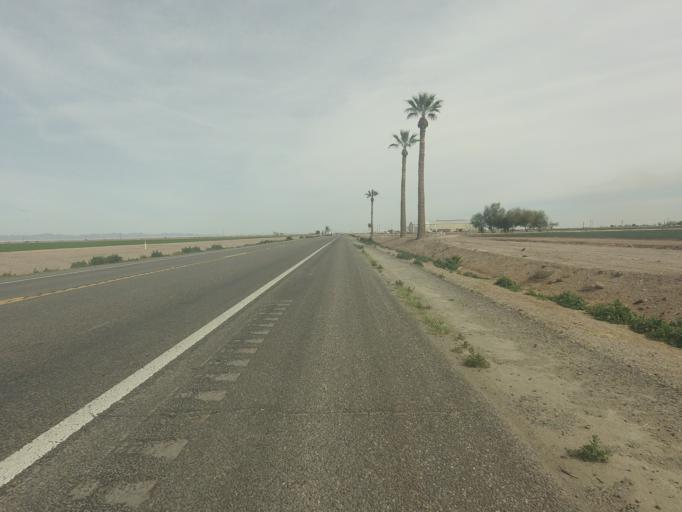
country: US
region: California
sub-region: Imperial County
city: Brawley
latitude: 32.9745
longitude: -115.4290
